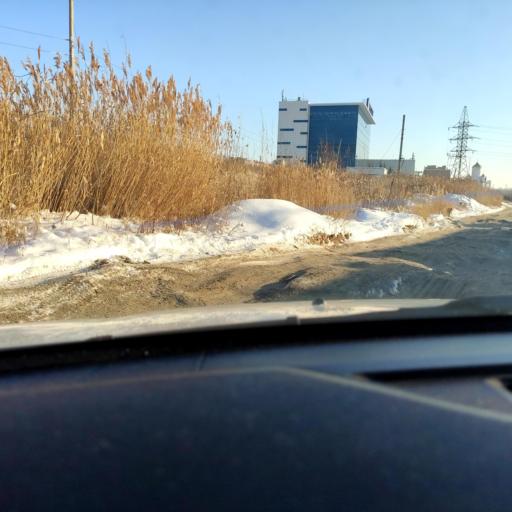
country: RU
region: Samara
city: Petra-Dubrava
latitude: 53.3201
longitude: 50.3012
